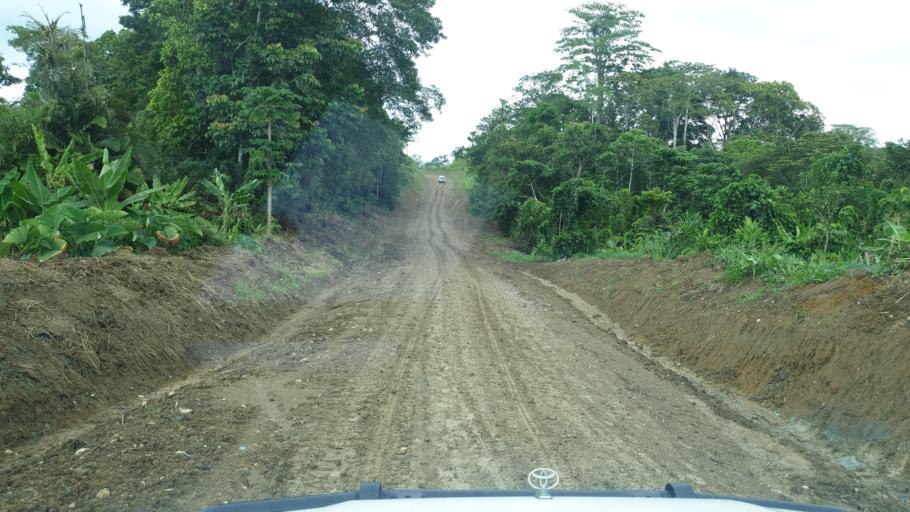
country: PG
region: Gulf
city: Kerema
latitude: -7.9860
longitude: 145.8344
